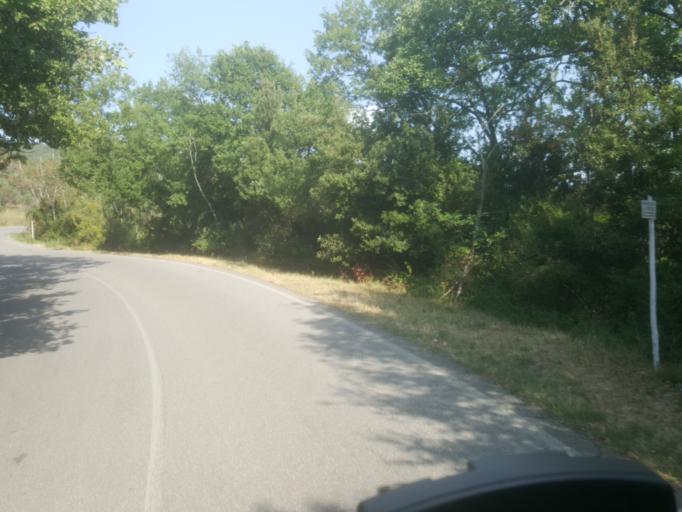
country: IT
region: Tuscany
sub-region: Province of Florence
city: Montaione
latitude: 43.4876
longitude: 10.8992
